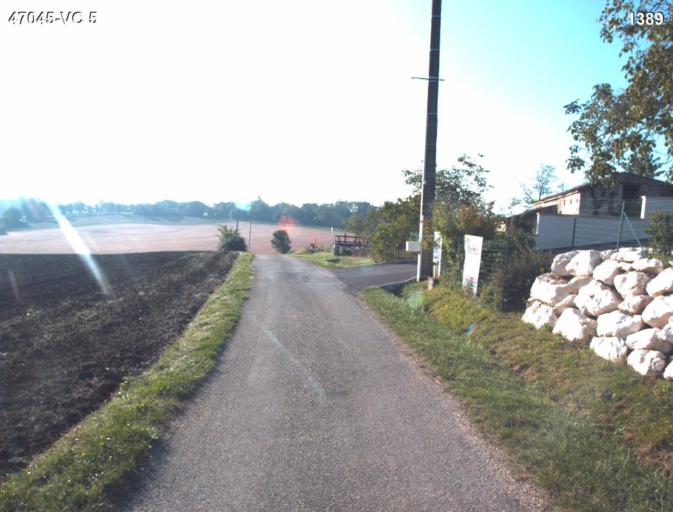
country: FR
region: Aquitaine
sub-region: Departement du Lot-et-Garonne
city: Nerac
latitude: 44.1418
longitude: 0.4051
